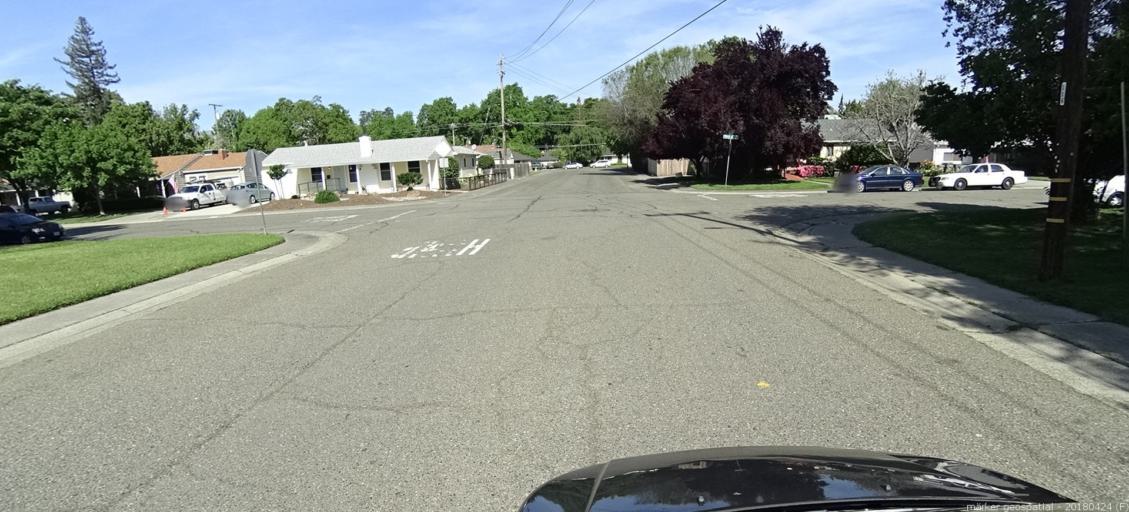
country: US
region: California
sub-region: Yolo County
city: West Sacramento
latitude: 38.5701
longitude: -121.5295
